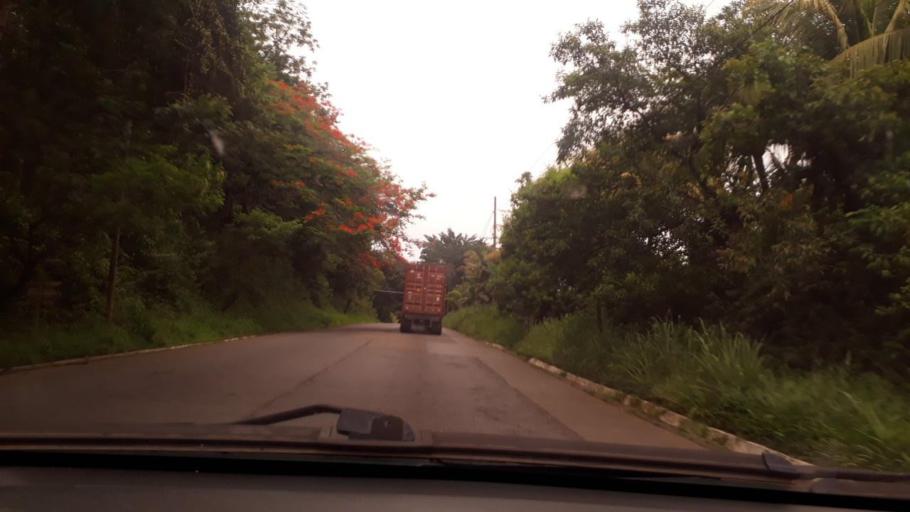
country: GT
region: Izabal
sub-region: Municipio de Puerto Barrios
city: Puerto Barrios
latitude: 15.5750
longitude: -88.6271
